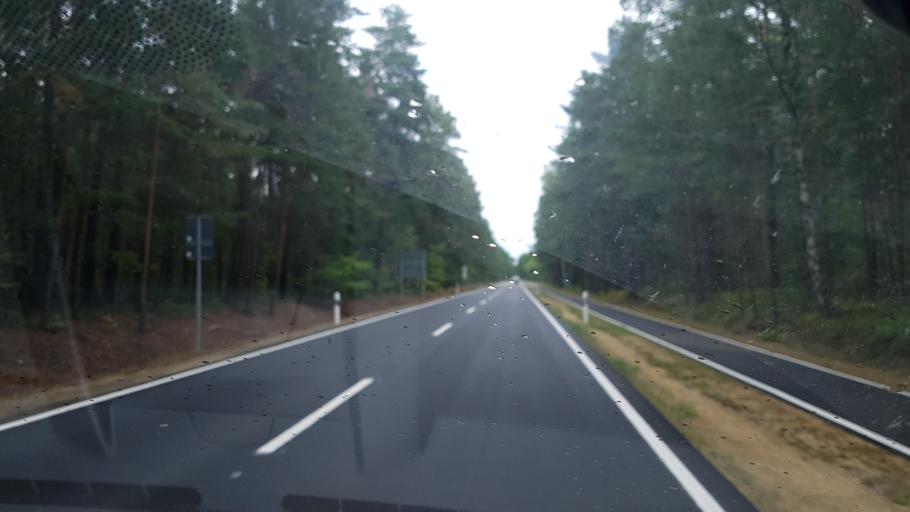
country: DE
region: Saxony
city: Niesky
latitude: 51.3076
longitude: 14.8166
